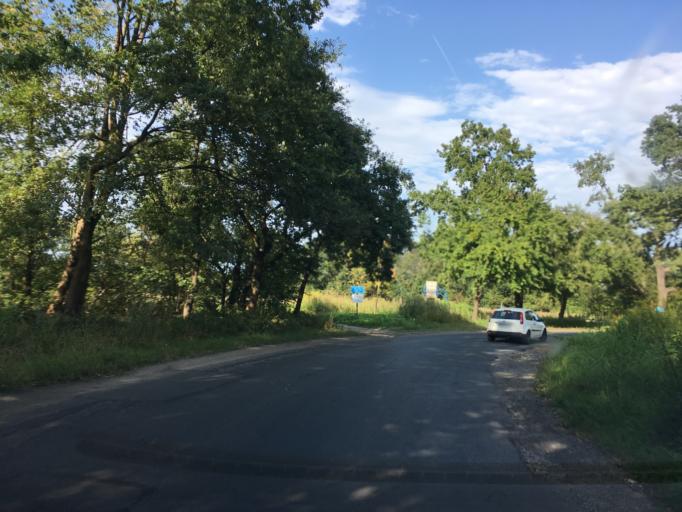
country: PL
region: Lower Silesian Voivodeship
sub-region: Powiat wroclawski
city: Radwanice
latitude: 51.0925
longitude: 17.0953
